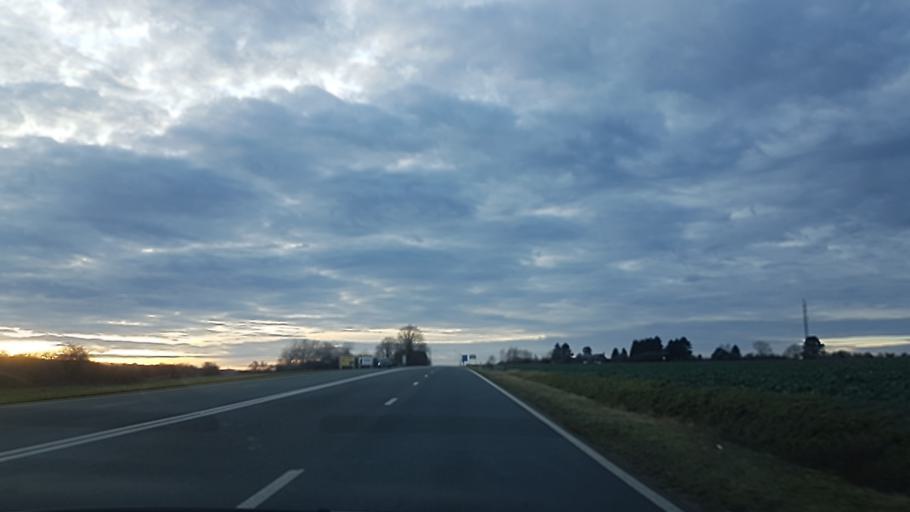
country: BE
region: Wallonia
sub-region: Province de Namur
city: Couvin
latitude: 50.0463
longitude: 4.4360
